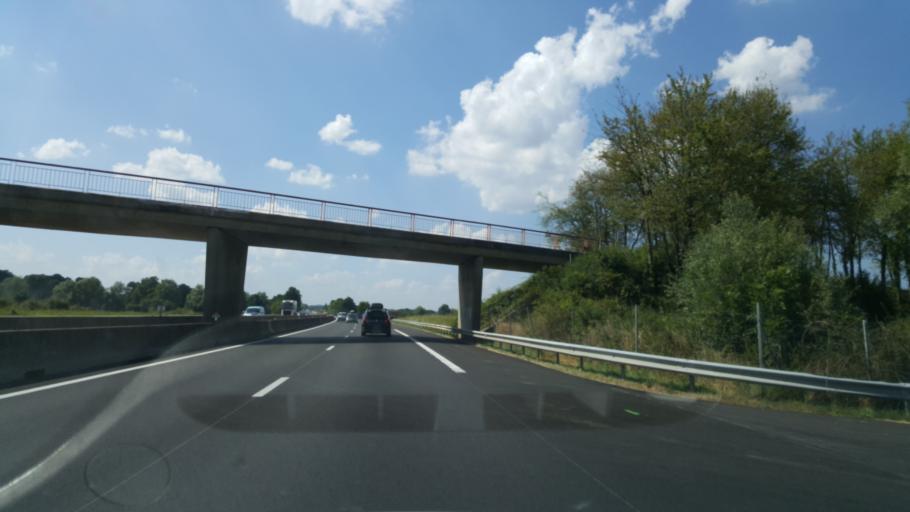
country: FR
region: Bourgogne
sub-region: Departement de la Cote-d'Or
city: Pouilly-en-Auxois
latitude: 47.2033
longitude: 4.6447
